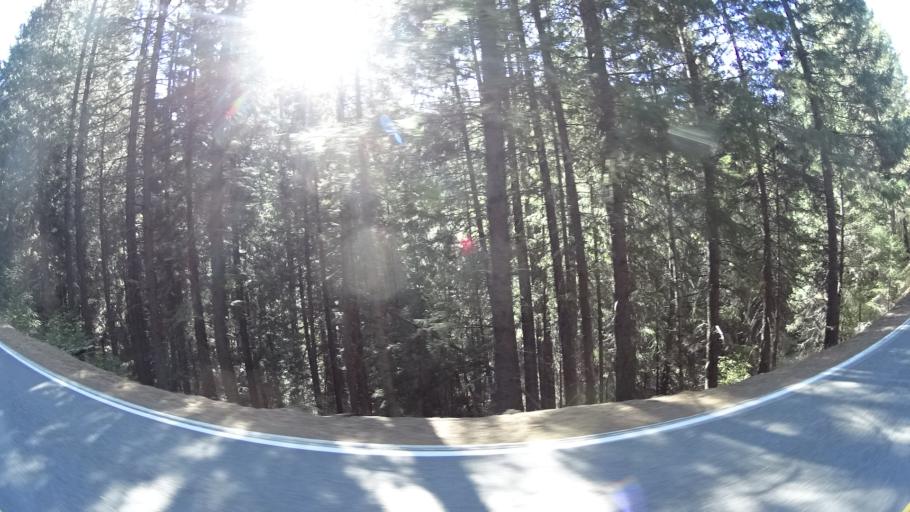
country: US
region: California
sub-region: Trinity County
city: Weaverville
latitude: 41.2226
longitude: -123.0193
